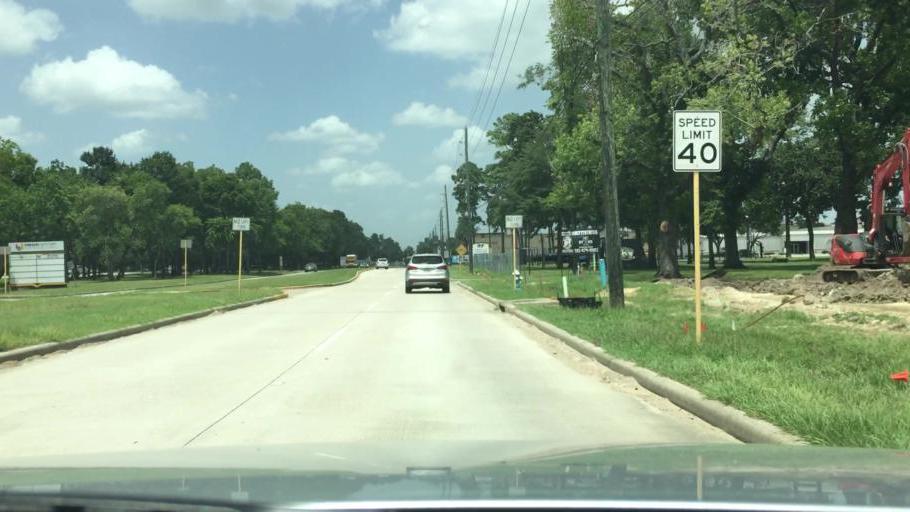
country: US
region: Texas
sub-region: Harris County
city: Hudson
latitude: 29.9646
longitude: -95.5307
